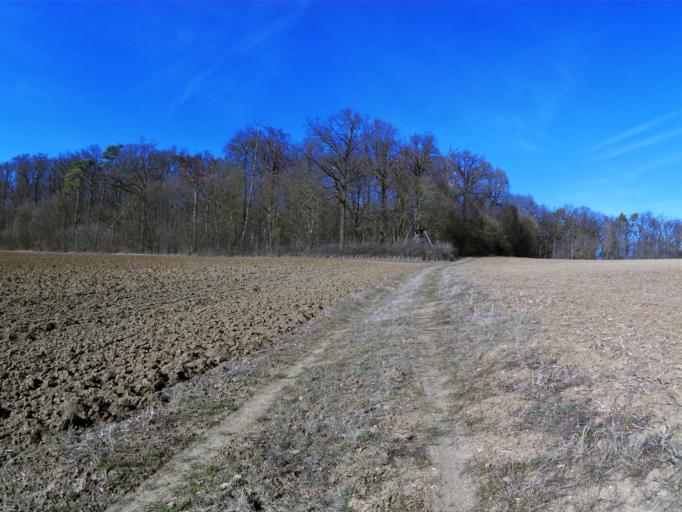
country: DE
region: Bavaria
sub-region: Regierungsbezirk Unterfranken
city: Estenfeld
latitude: 49.8518
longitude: 9.9975
